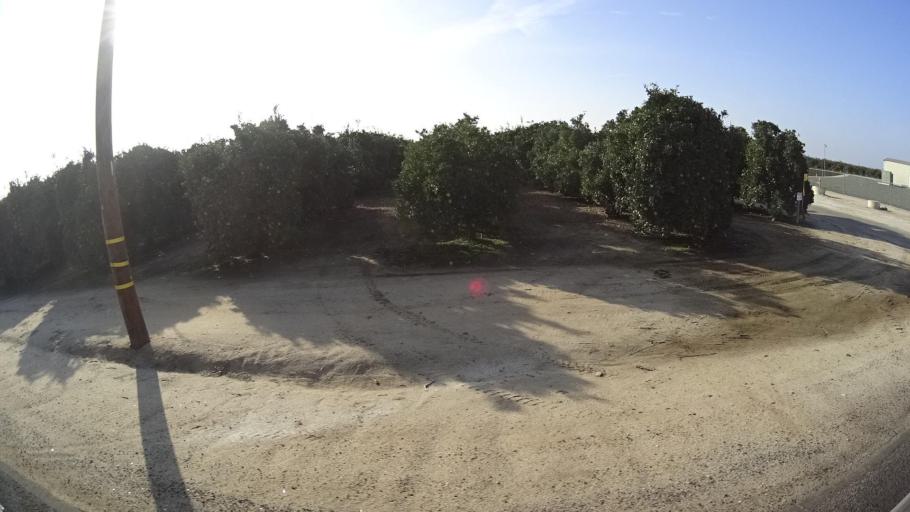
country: US
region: California
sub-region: Kern County
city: McFarland
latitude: 35.6746
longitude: -119.1781
